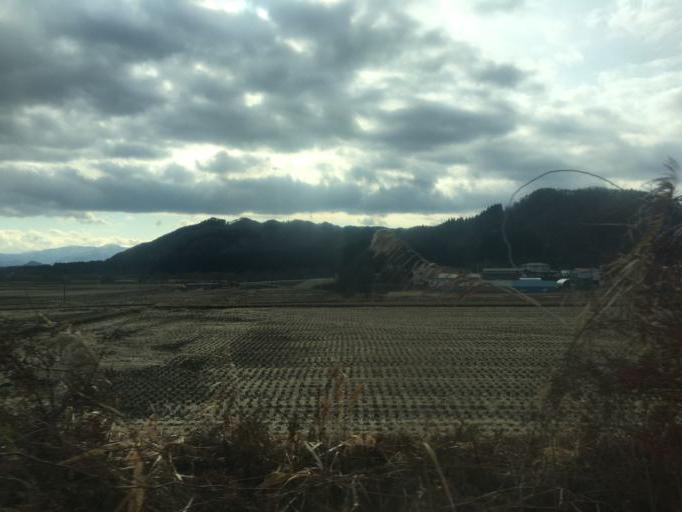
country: JP
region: Akita
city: Odate
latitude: 40.2730
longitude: 140.4714
